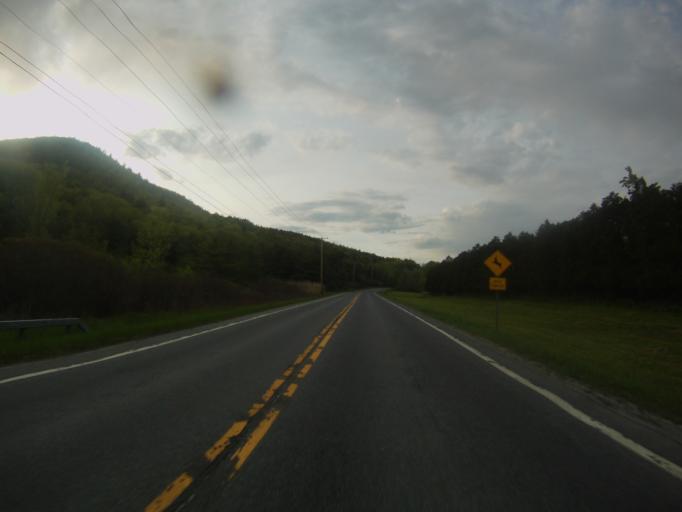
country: US
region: New York
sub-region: Essex County
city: Ticonderoga
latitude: 43.9191
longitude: -73.4204
